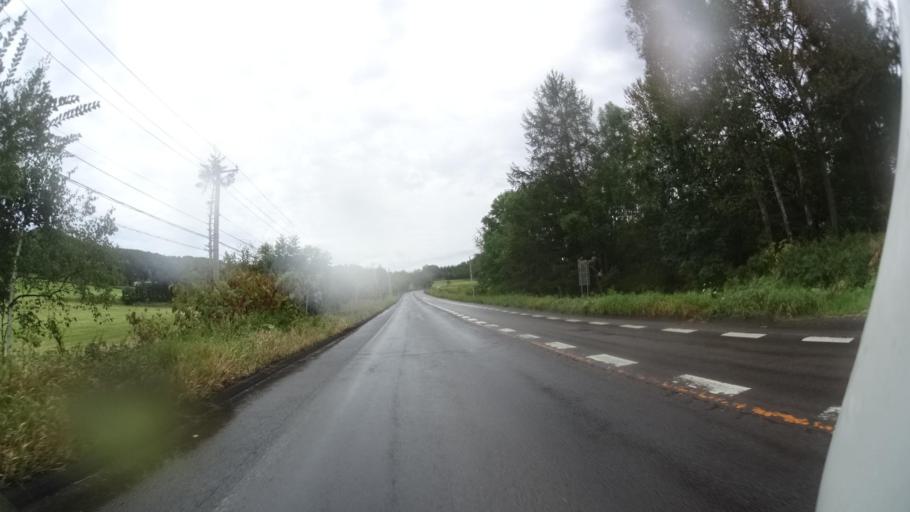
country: JP
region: Hokkaido
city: Kitami
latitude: 44.0954
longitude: 143.7391
